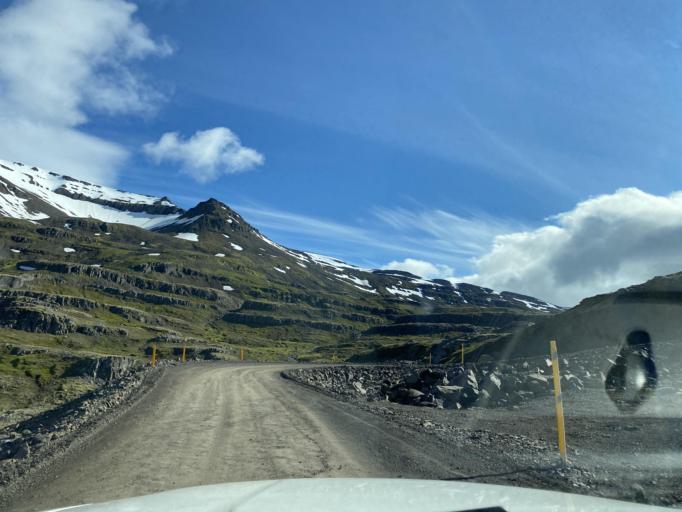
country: IS
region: East
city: Eskifjoerdur
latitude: 65.1780
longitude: -14.0973
